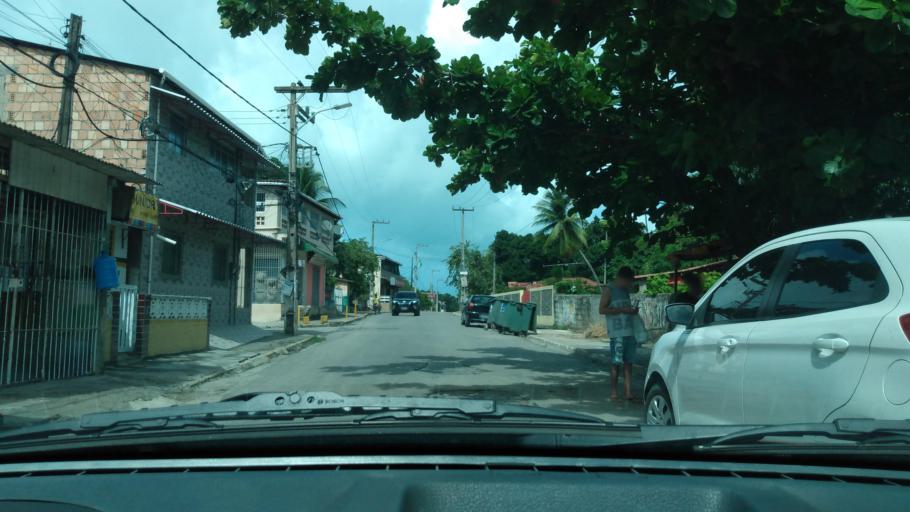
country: BR
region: Pernambuco
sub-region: Cabo De Santo Agostinho
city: Cabo
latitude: -8.3528
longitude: -34.9568
